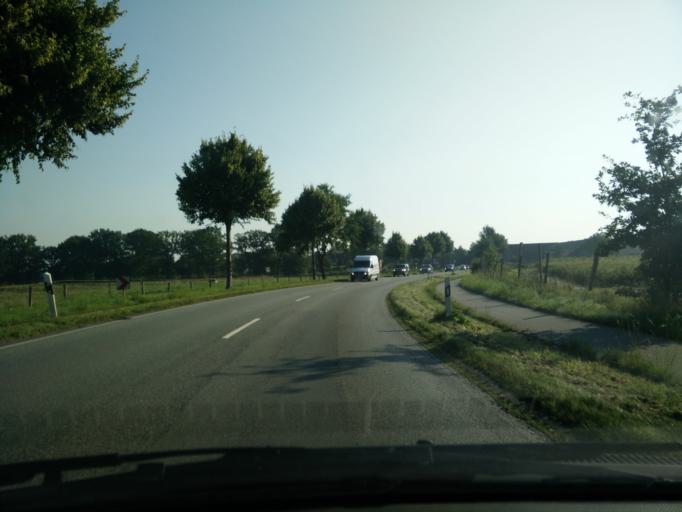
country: DE
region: Schleswig-Holstein
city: Tornesch
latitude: 53.7080
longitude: 9.7379
